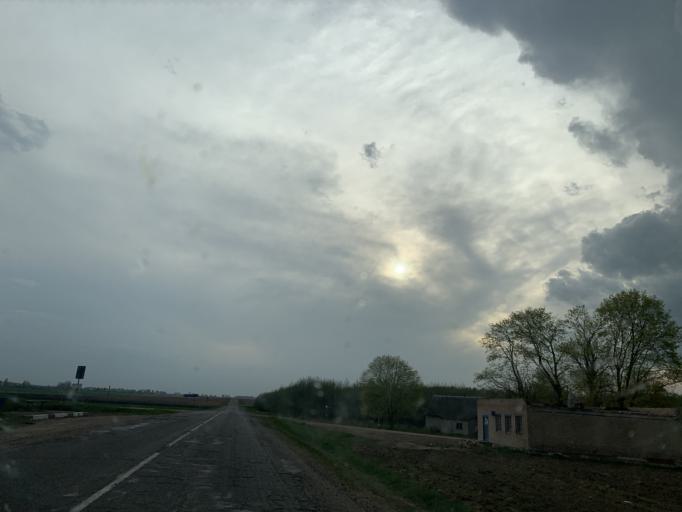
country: BY
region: Minsk
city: Kapyl'
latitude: 53.3036
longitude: 27.0626
